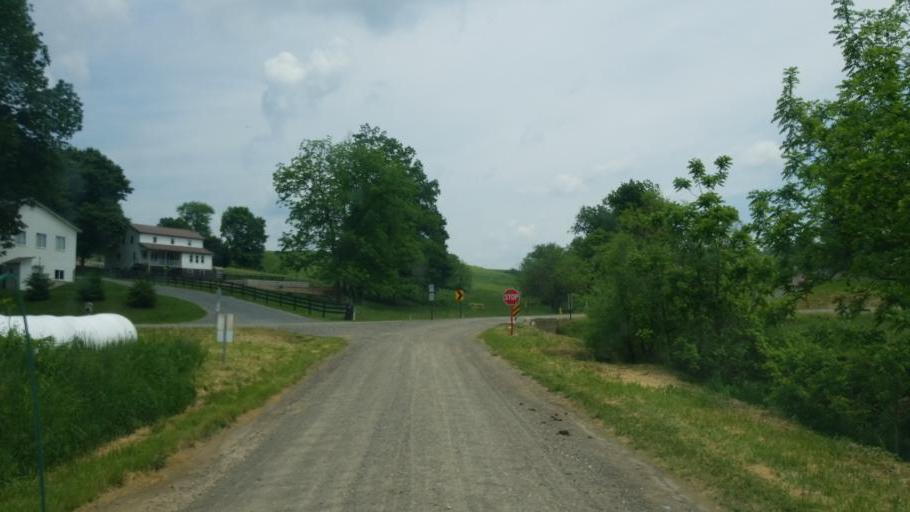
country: US
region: Ohio
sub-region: Holmes County
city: Millersburg
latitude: 40.4834
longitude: -81.7952
